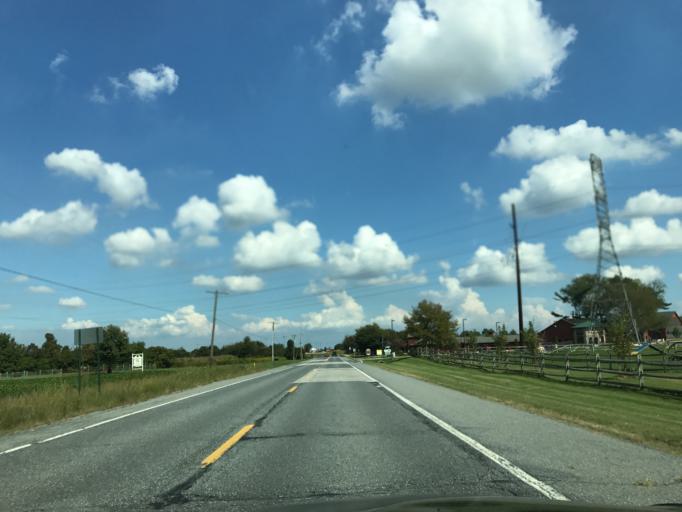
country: US
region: Delaware
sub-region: New Castle County
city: Middletown
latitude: 39.4233
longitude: -75.7677
